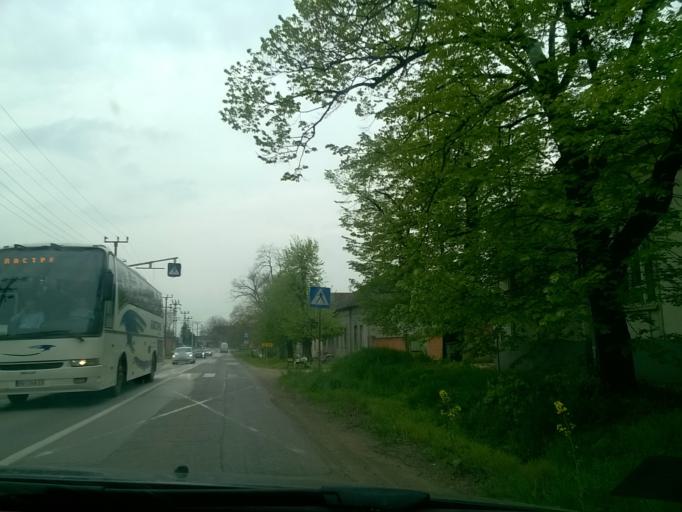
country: RS
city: Hrtkovci
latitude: 44.8778
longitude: 19.7699
